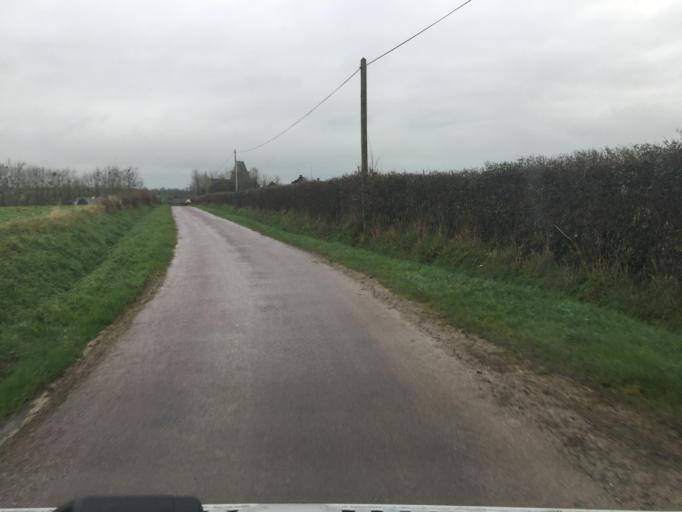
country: FR
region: Lower Normandy
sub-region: Departement de la Manche
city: Sainte-Mere-Eglise
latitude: 49.4349
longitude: -1.2598
